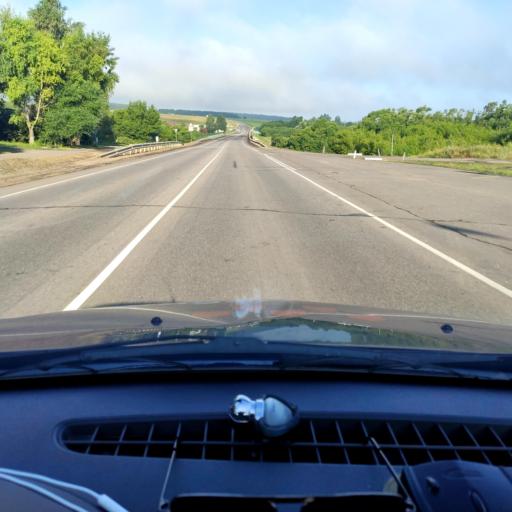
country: RU
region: Orjol
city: Livny
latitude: 52.4478
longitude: 37.4736
